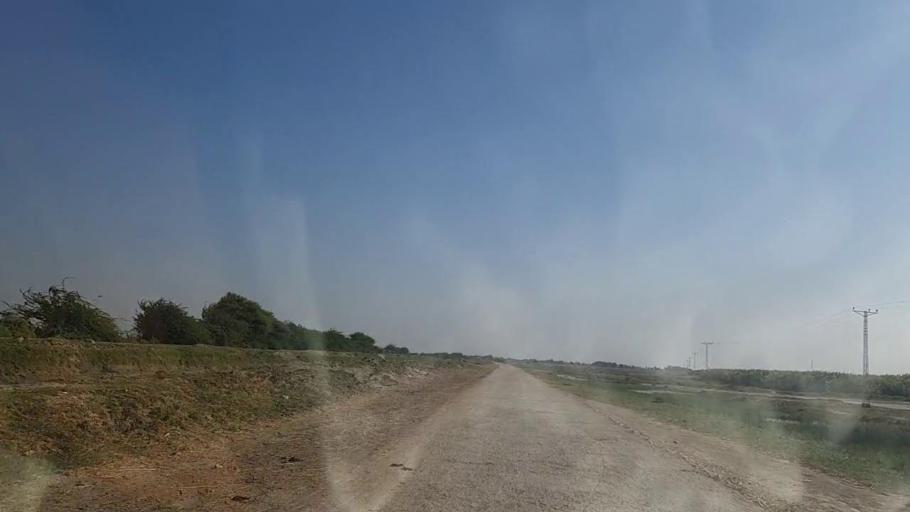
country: PK
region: Sindh
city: Mirpur Batoro
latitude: 24.6115
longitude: 68.1683
